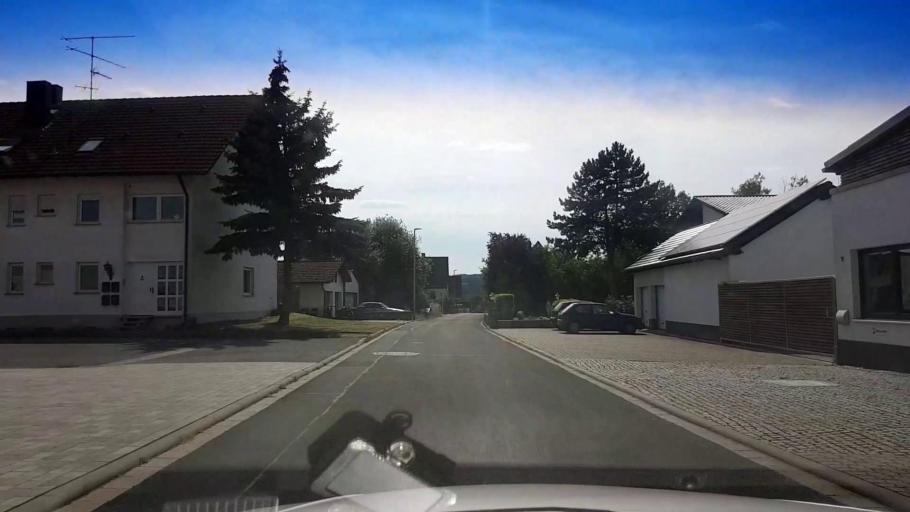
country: DE
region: Bavaria
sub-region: Regierungsbezirk Unterfranken
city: Stettfeld
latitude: 49.9698
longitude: 10.7263
